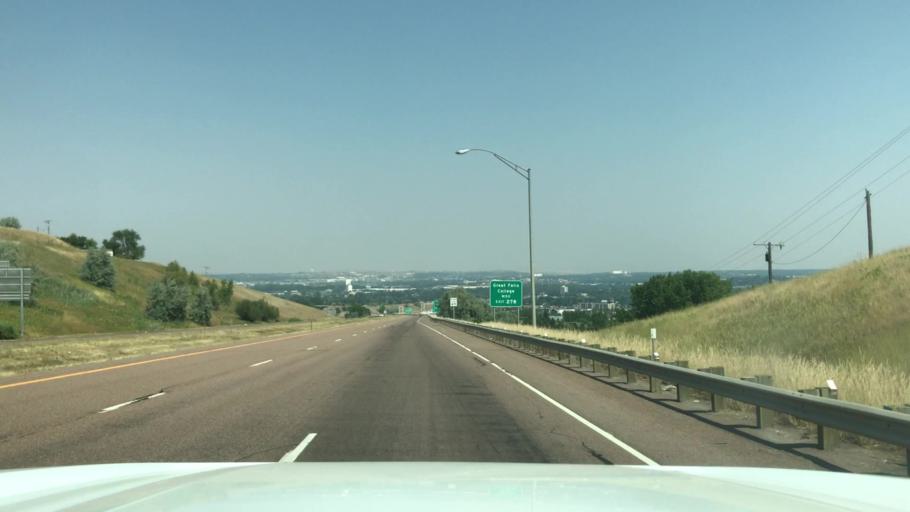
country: US
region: Montana
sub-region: Cascade County
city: Great Falls
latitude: 47.4751
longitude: -111.3565
